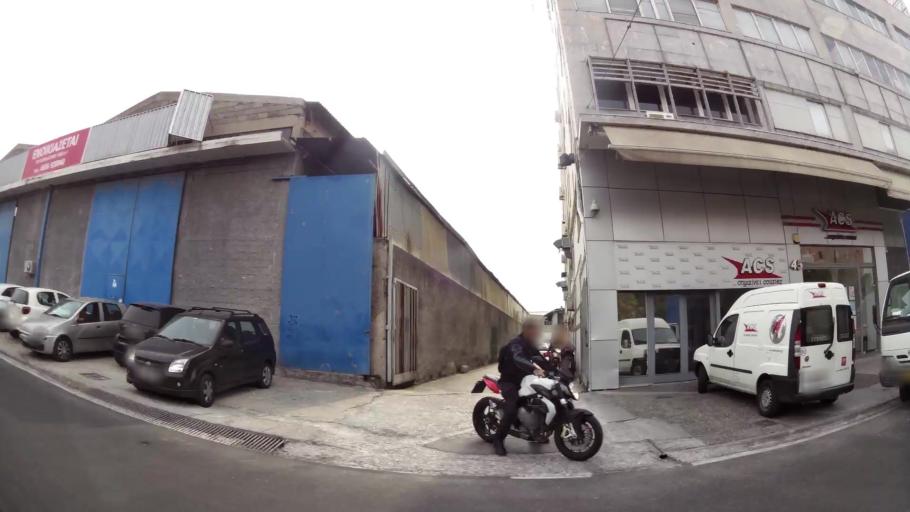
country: GR
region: Attica
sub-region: Nomarchia Athinas
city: Tavros
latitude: 37.9760
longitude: 23.6888
